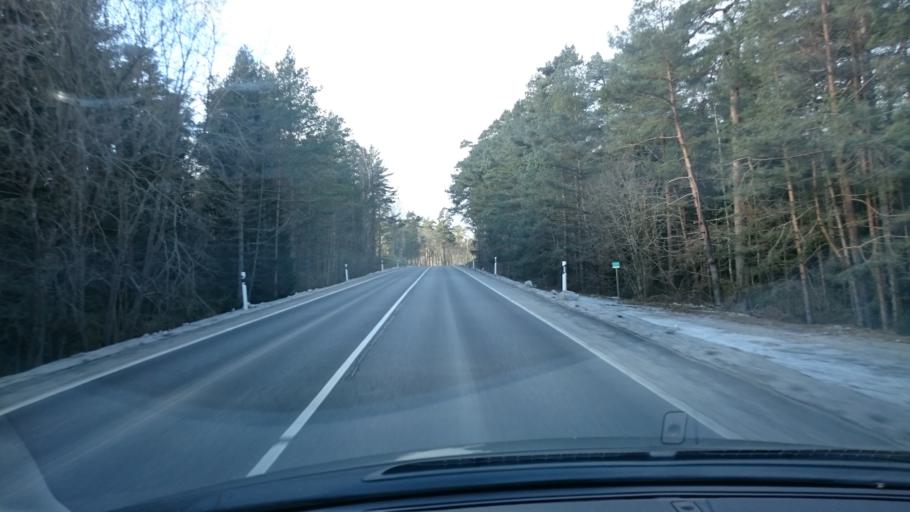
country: EE
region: Harju
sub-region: Keila linn
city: Keila
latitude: 59.3976
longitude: 24.2652
